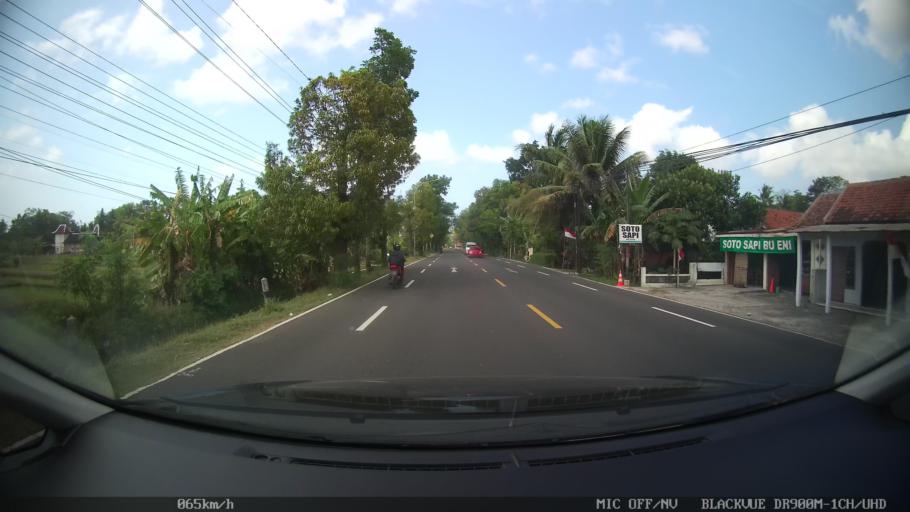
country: ID
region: Daerah Istimewa Yogyakarta
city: Srandakan
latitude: -7.8830
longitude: 110.1315
